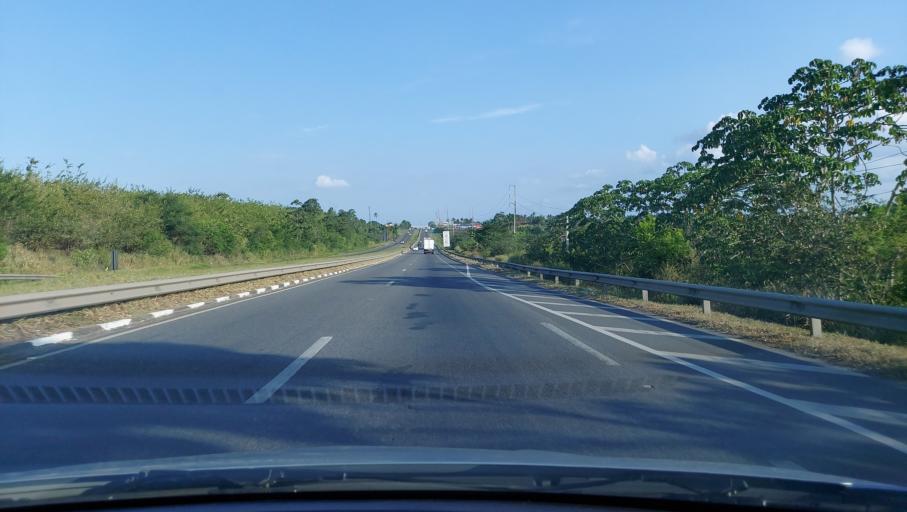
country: BR
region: Bahia
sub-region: Conceicao Do Jacuipe
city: Conceicao do Jacuipe
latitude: -12.3626
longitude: -38.8223
